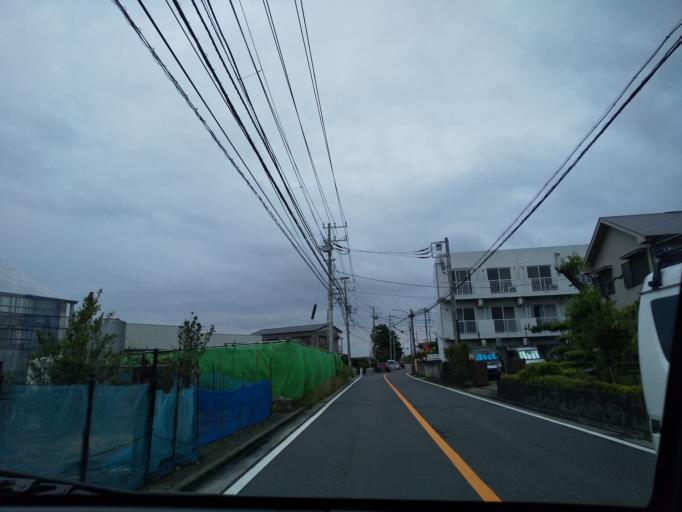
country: JP
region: Kanagawa
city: Fujisawa
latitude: 35.3932
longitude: 139.5056
